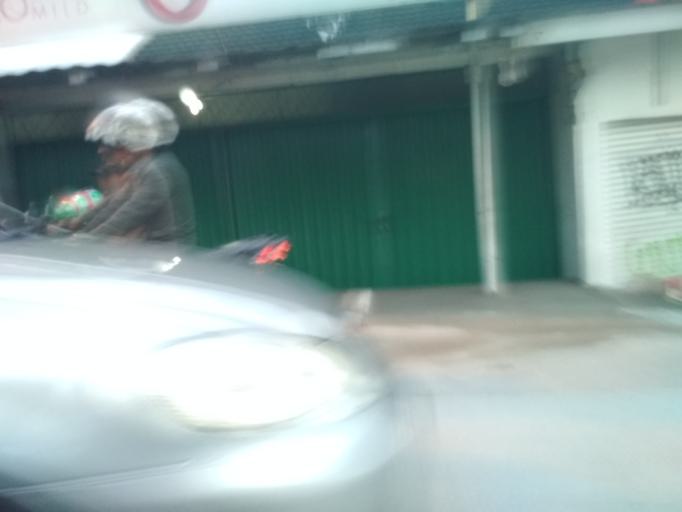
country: ID
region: West Java
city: Caringin
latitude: -6.7124
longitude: 106.8211
